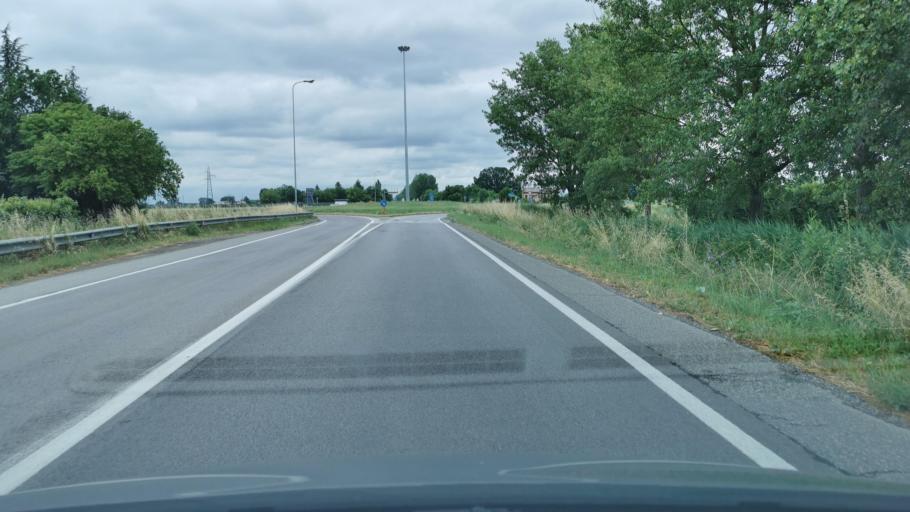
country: IT
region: Emilia-Romagna
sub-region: Provincia di Ravenna
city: Cotignola
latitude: 44.3818
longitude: 11.9510
